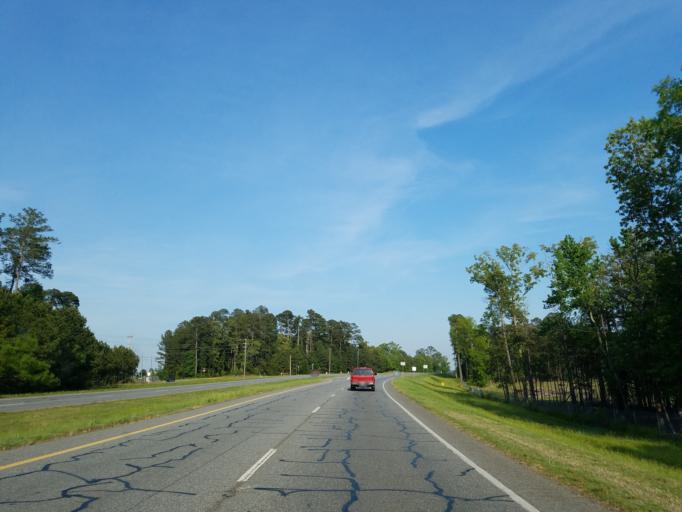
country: US
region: Georgia
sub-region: Floyd County
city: Rome
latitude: 34.3995
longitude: -85.2081
